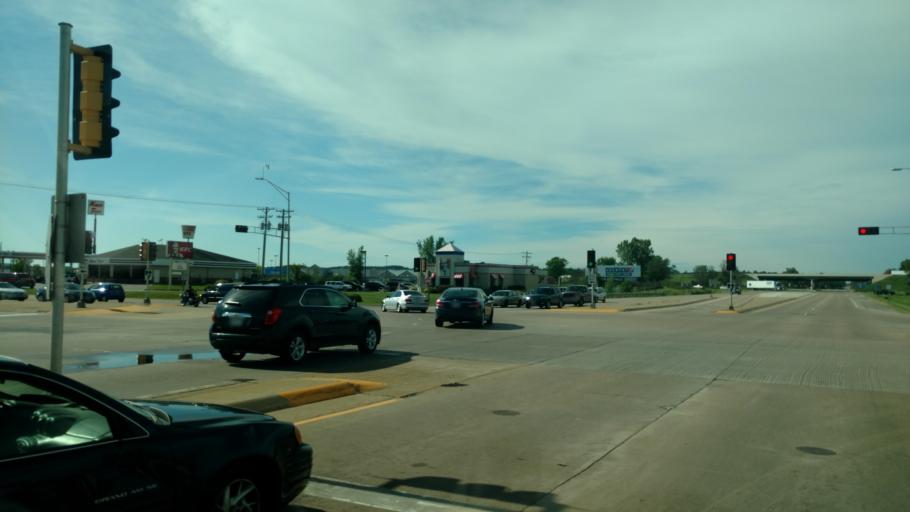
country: US
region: Wisconsin
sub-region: Monroe County
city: Tomah
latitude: 44.0177
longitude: -90.5050
